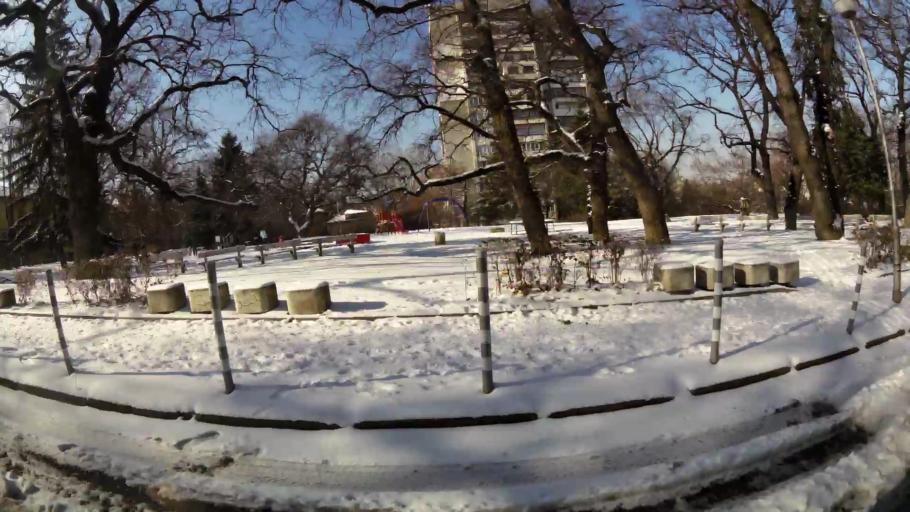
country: BG
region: Sofia-Capital
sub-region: Stolichna Obshtina
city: Sofia
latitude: 42.6768
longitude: 23.3293
